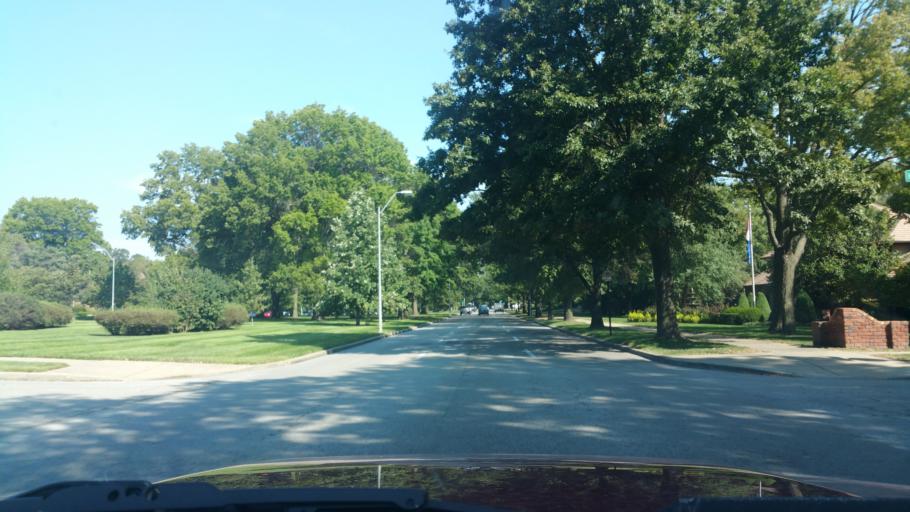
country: US
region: Kansas
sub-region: Johnson County
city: Mission Hills
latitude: 39.0186
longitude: -94.6017
